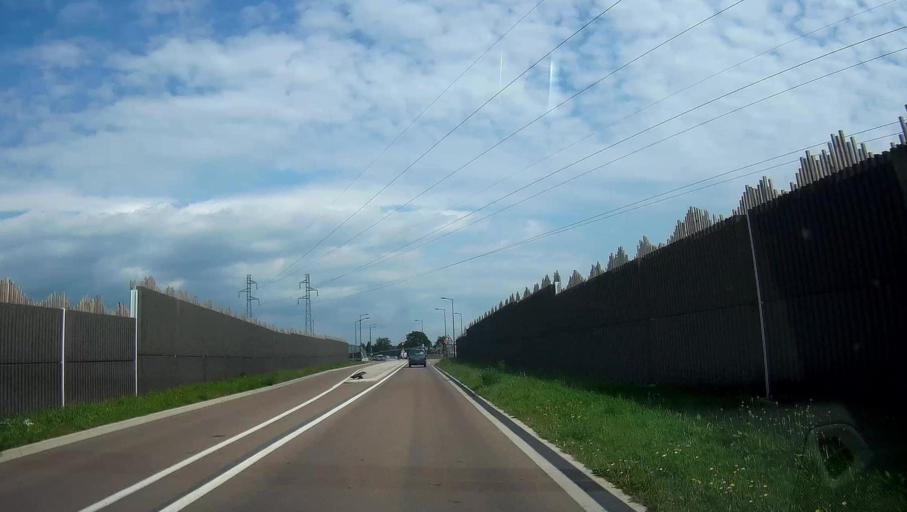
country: FR
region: Bourgogne
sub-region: Departement de la Cote-d'Or
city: Beaune
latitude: 47.0260
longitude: 4.8589
